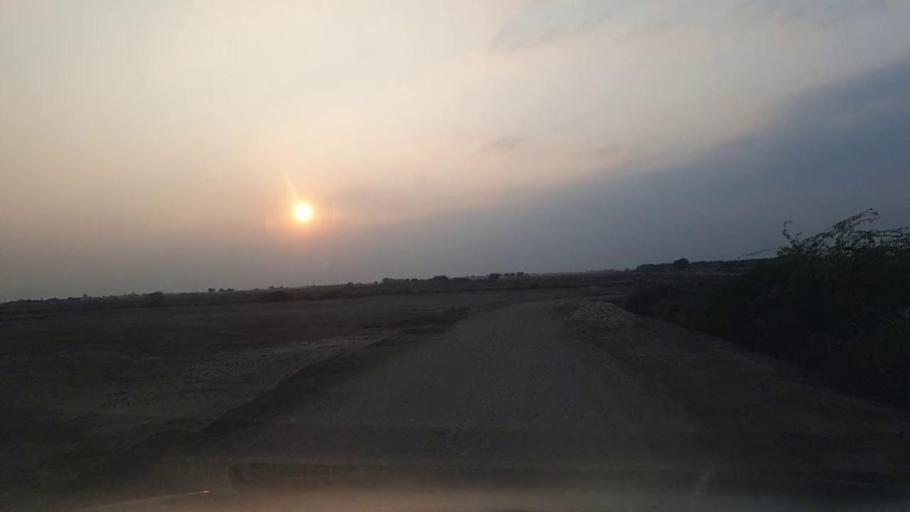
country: PK
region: Sindh
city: Jati
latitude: 24.5294
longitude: 68.4088
